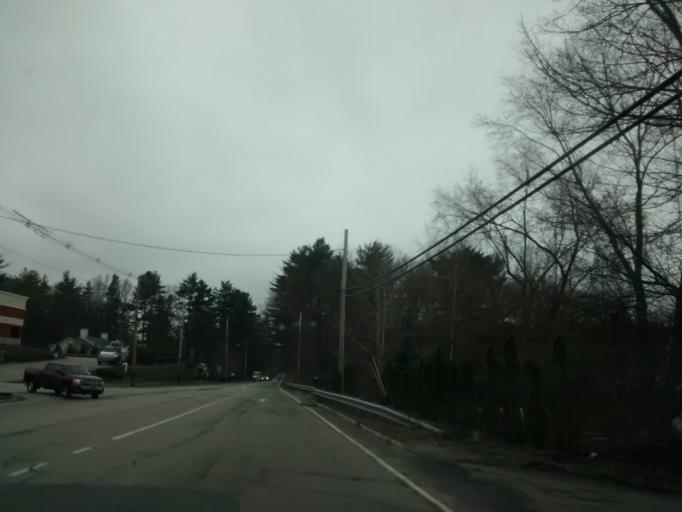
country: US
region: Massachusetts
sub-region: Middlesex County
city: Hopkinton
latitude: 42.2104
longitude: -71.5519
